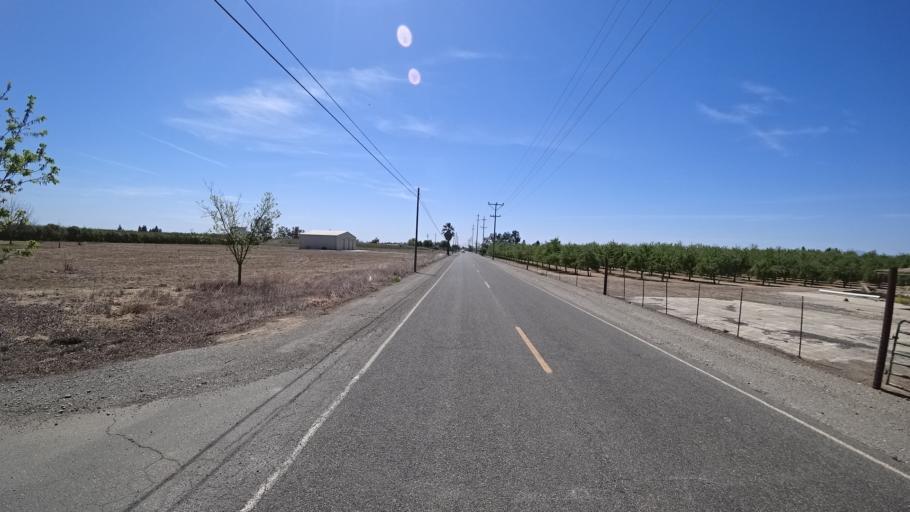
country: US
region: California
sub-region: Glenn County
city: Orland
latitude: 39.7163
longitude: -122.1784
